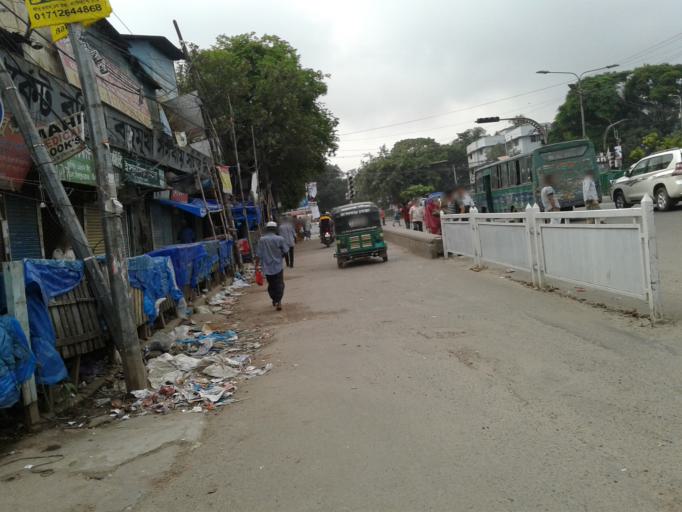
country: BD
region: Dhaka
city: Azimpur
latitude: 23.7329
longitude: 90.3851
